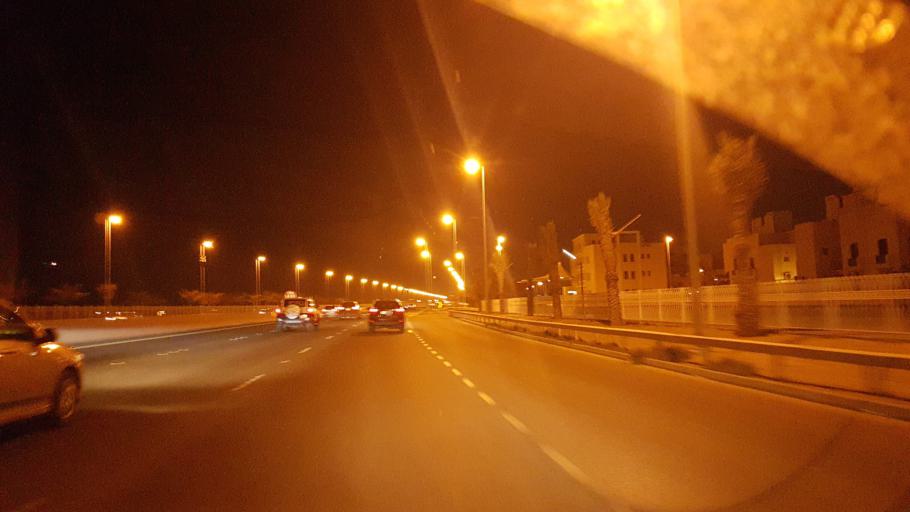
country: BH
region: Muharraq
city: Al Hadd
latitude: 26.2685
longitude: 50.6618
